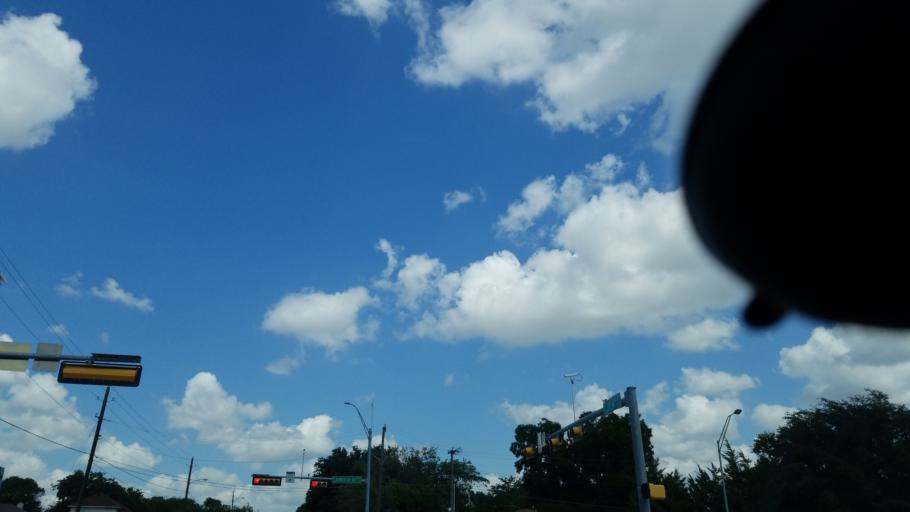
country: US
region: Texas
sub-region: Dallas County
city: Grand Prairie
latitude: 32.7052
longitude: -96.9854
